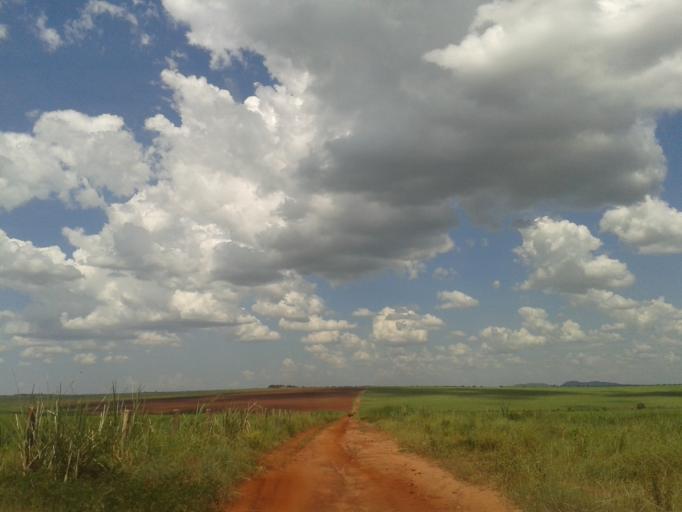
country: BR
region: Minas Gerais
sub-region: Santa Vitoria
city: Santa Vitoria
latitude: -19.1782
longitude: -50.4432
